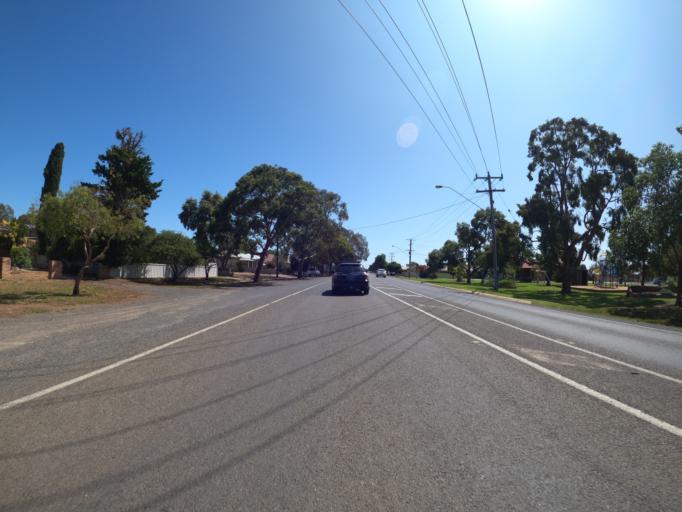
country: AU
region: Victoria
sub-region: Moira
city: Yarrawonga
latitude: -36.0154
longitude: 146.0123
